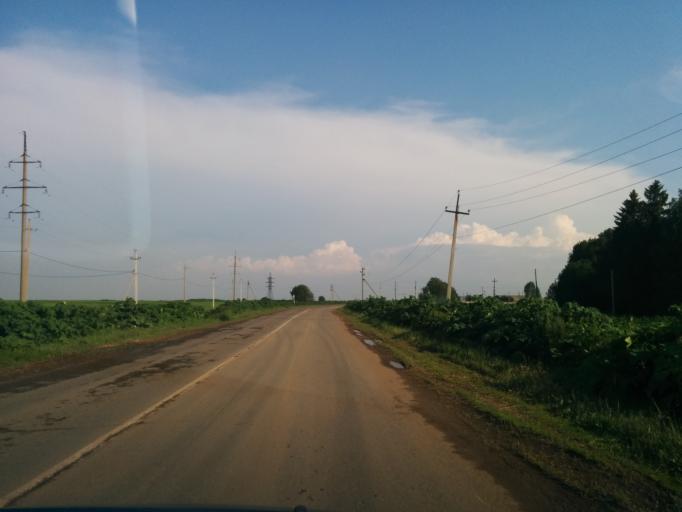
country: RU
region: Perm
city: Polazna
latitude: 58.2241
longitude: 56.2958
